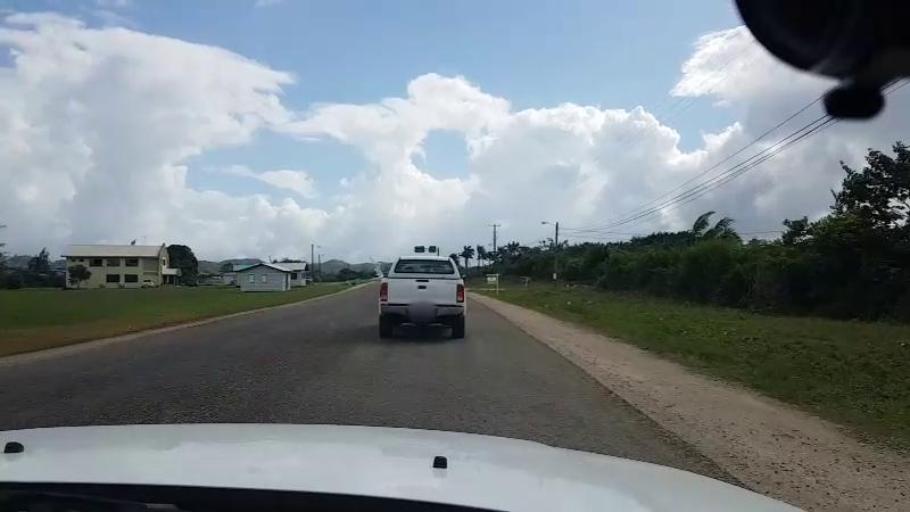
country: BZ
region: Cayo
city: Belmopan
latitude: 17.2431
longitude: -88.7830
